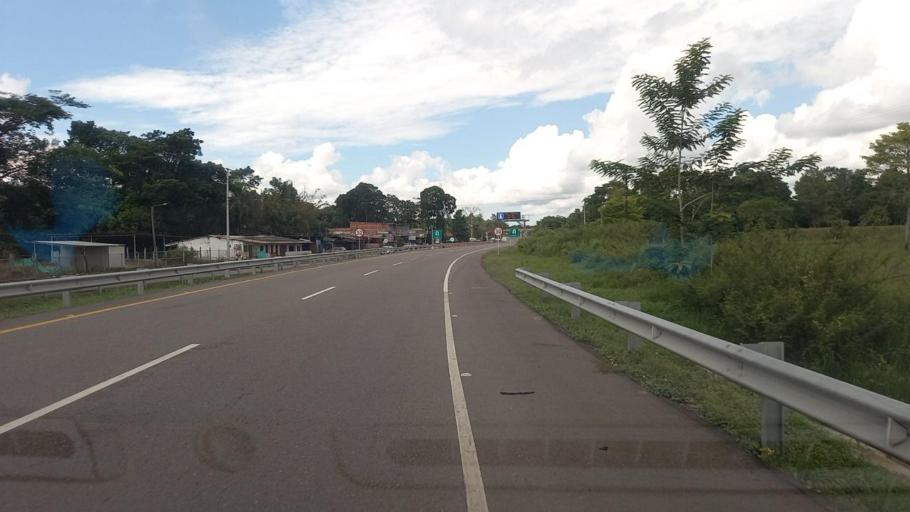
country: CO
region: Santander
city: Sabana de Torres
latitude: 7.1343
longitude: -73.5512
